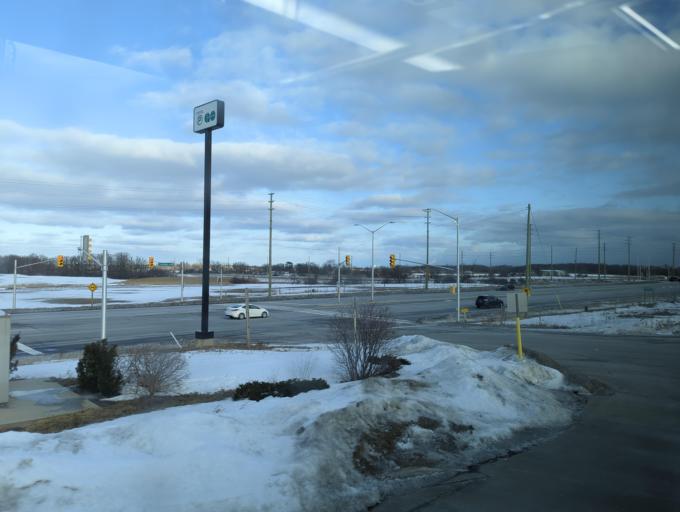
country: CA
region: Ontario
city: Oakville
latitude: 43.5059
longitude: -79.7449
